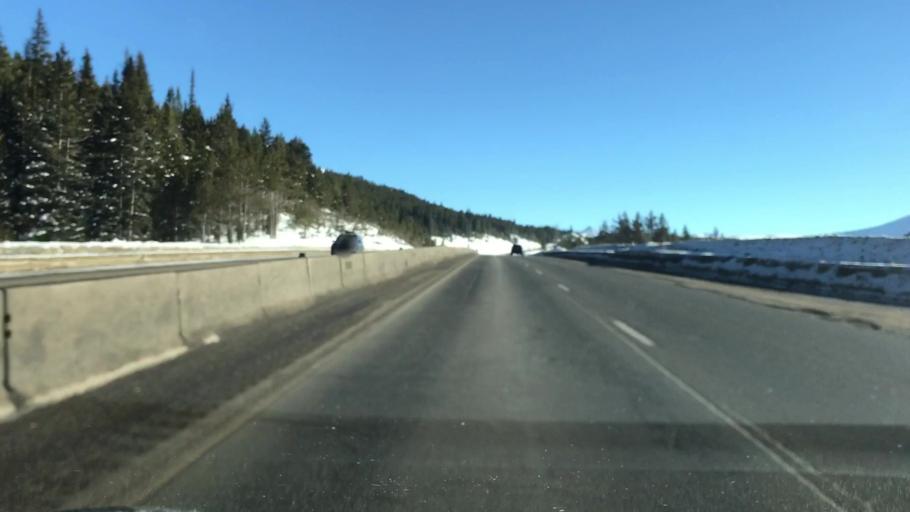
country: US
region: Colorado
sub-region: Summit County
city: Frisco
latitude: 39.5532
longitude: -106.2255
